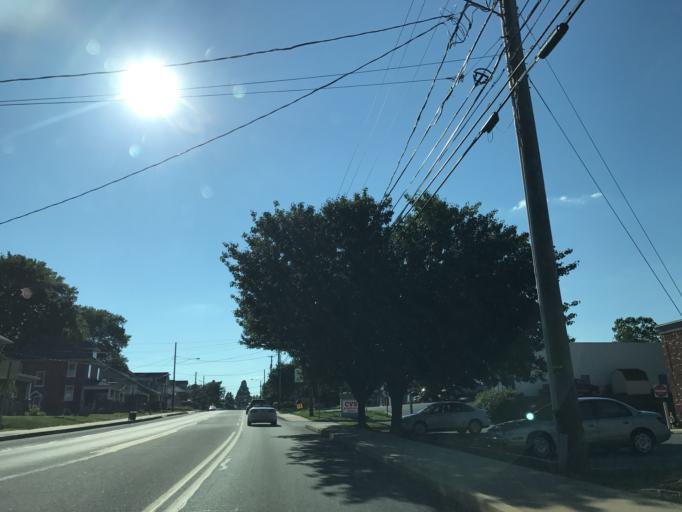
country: US
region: Pennsylvania
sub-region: Lancaster County
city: Mount Joy
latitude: 40.1130
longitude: -76.5160
